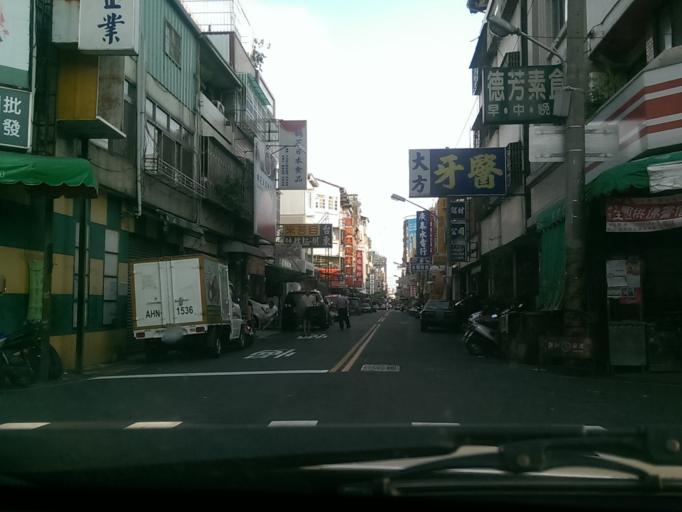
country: TW
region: Taiwan
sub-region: Taichung City
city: Taichung
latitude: 24.1491
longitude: 120.6588
